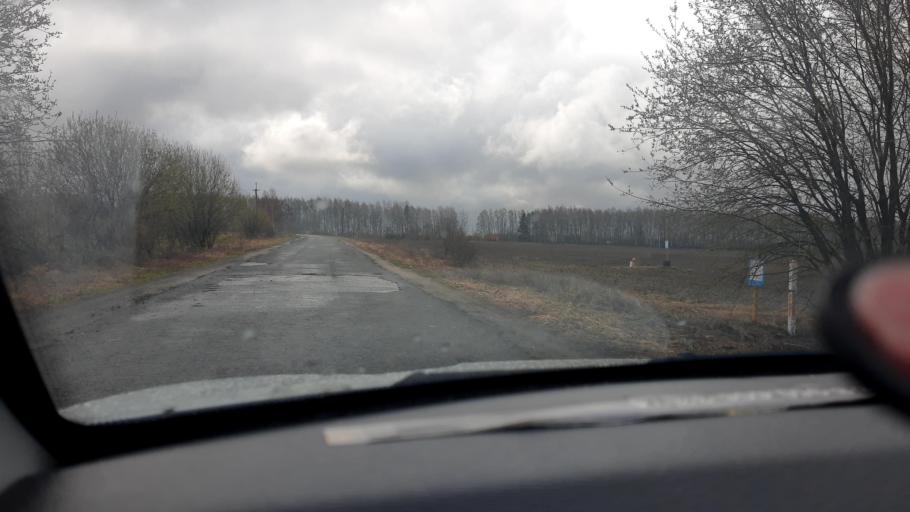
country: RU
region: Nizjnij Novgorod
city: Burevestnik
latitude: 56.1587
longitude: 43.6997
